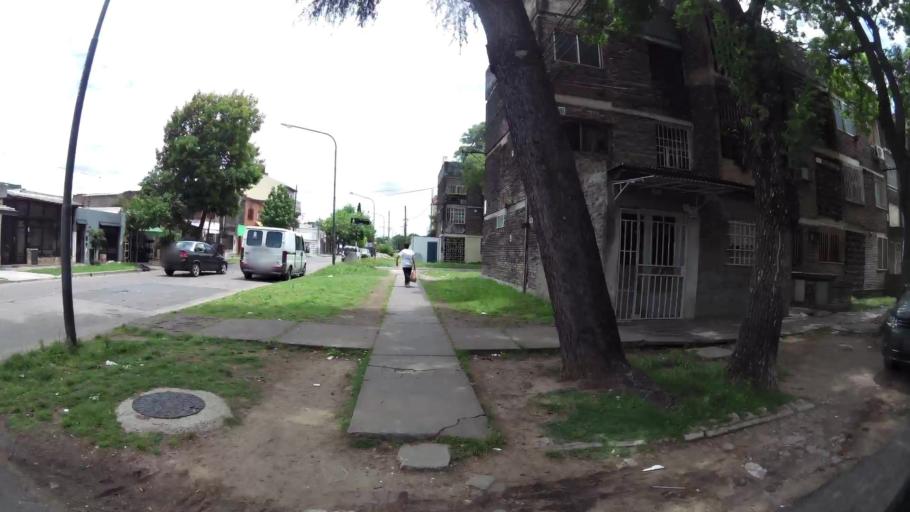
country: AR
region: Santa Fe
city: Gobernador Galvez
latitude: -32.9933
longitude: -60.6300
